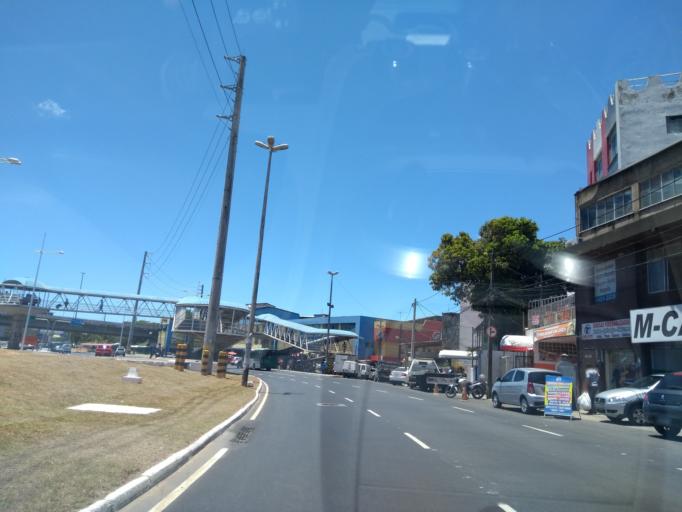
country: BR
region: Bahia
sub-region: Salvador
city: Salvador
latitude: -12.9752
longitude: -38.4603
